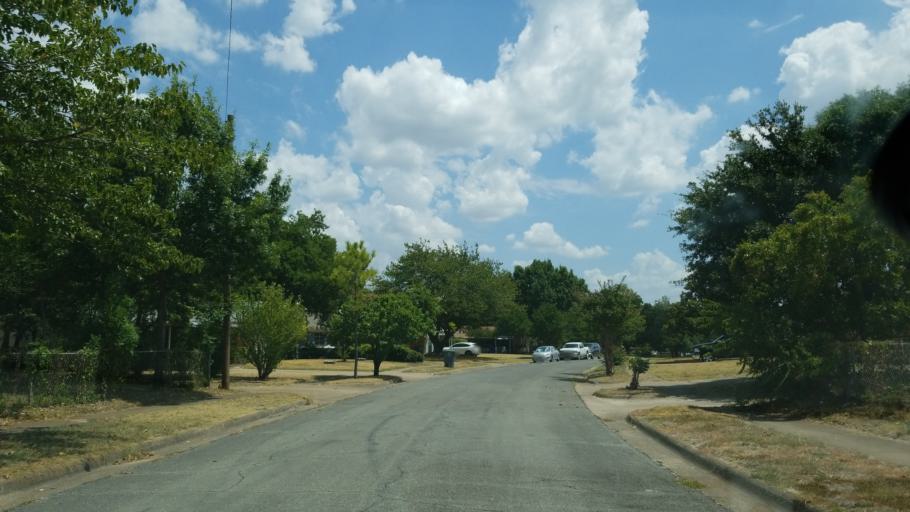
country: US
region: Texas
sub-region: Dallas County
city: Cockrell Hill
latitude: 32.7217
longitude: -96.8972
